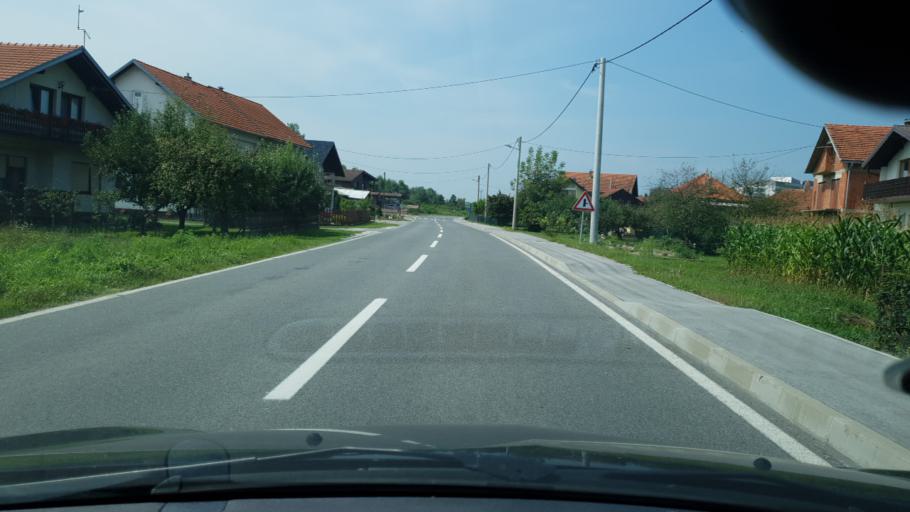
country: HR
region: Krapinsko-Zagorska
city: Zabok
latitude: 46.0201
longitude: 15.9479
